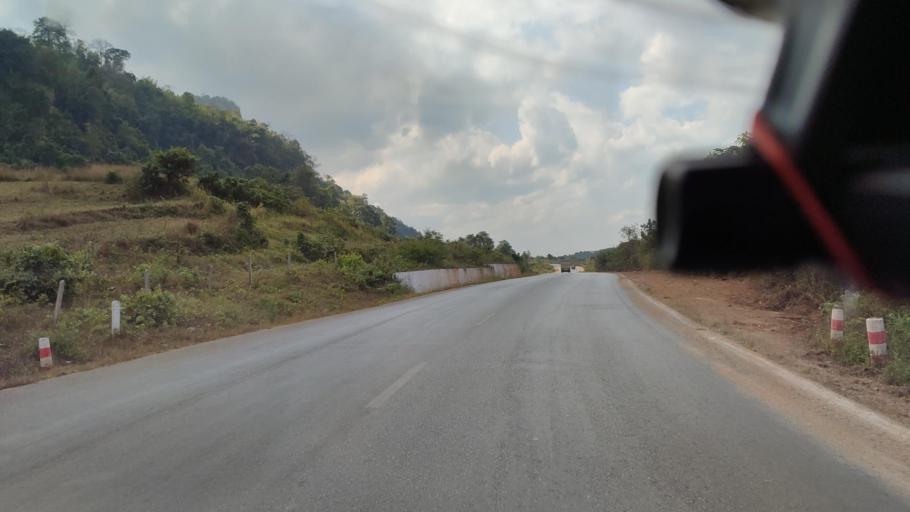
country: MM
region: Shan
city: Lashio
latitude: 22.9956
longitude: 97.7169
